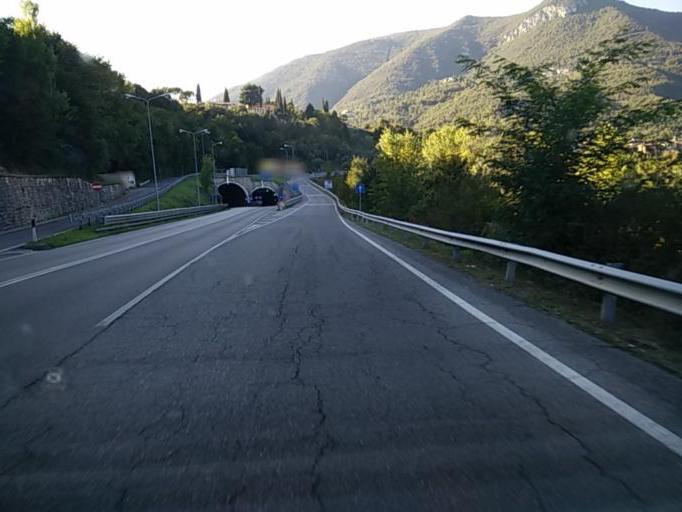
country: IT
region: Lombardy
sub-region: Provincia di Brescia
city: Roe Volciano
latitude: 45.6059
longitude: 10.4866
